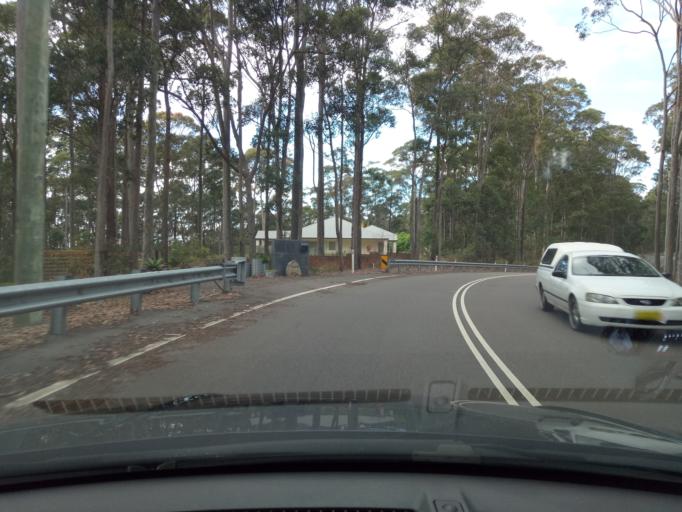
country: AU
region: New South Wales
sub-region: Wyong Shire
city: Tumbi Vmbi
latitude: -33.3872
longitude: 151.4377
